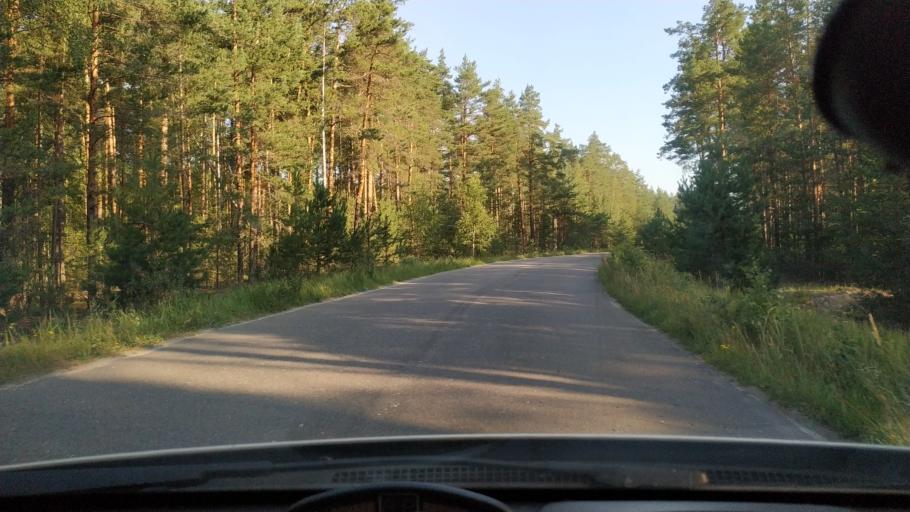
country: RU
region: Moskovskaya
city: Roshal'
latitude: 55.6533
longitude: 39.7994
